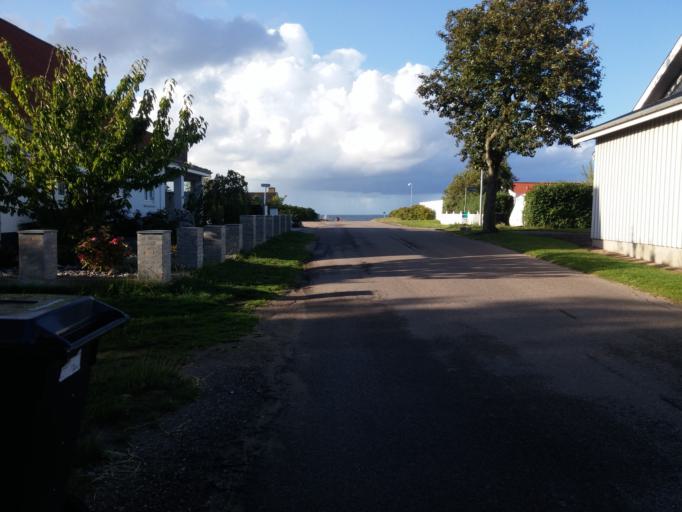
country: DK
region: Zealand
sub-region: Kalundborg Kommune
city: Svebolle
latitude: 55.7532
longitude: 11.3383
